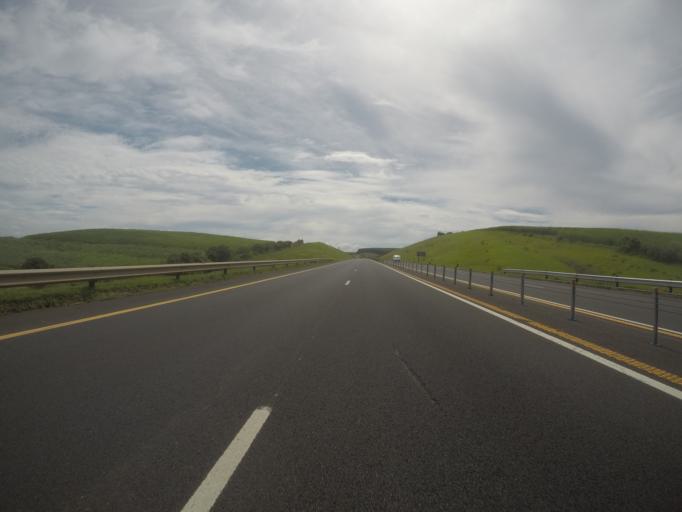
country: ZA
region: KwaZulu-Natal
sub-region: uThungulu District Municipality
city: Eshowe
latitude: -29.0499
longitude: 31.6384
